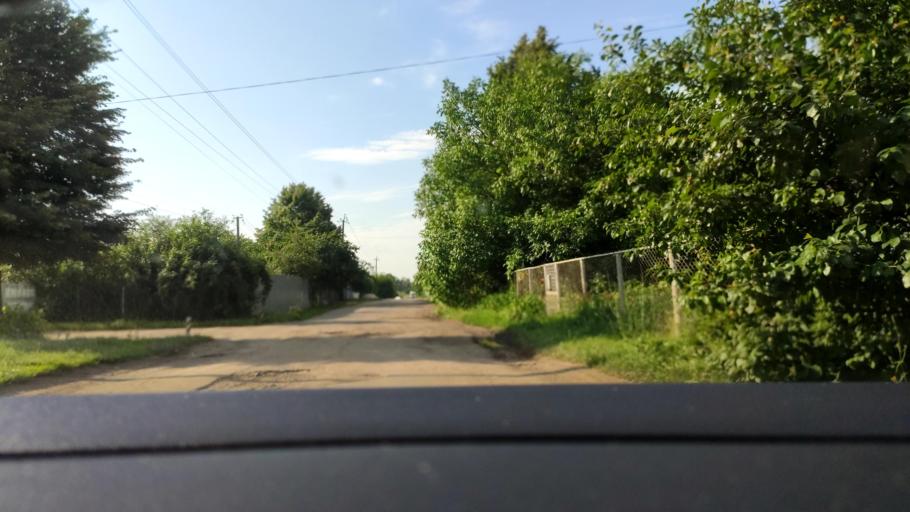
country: RU
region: Voronezj
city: Maslovka
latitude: 51.5366
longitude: 39.3361
